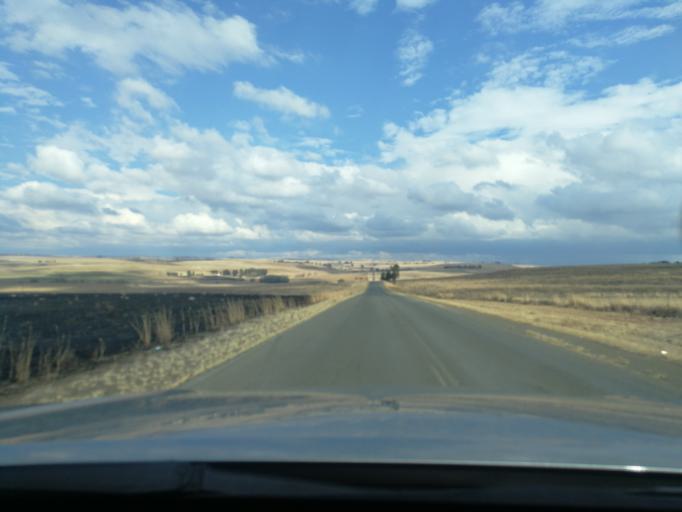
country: ZA
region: Orange Free State
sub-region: Fezile Dabi District Municipality
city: Frankfort
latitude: -27.4577
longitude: 28.5201
